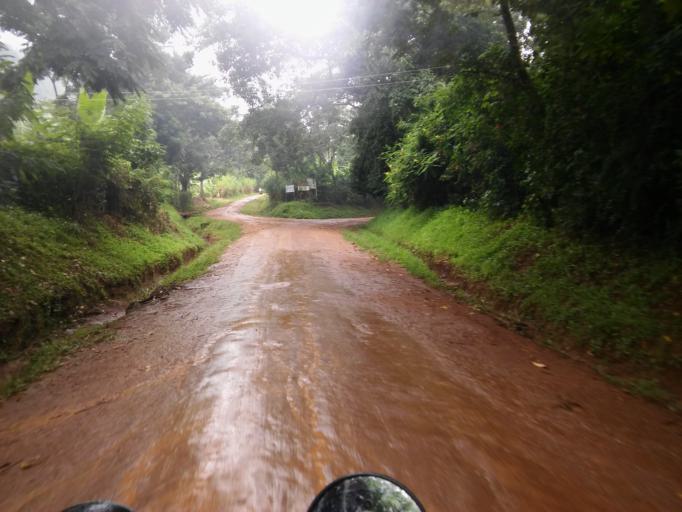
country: UG
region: Eastern Region
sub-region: Bududa District
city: Bududa
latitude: 1.0001
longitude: 34.2519
